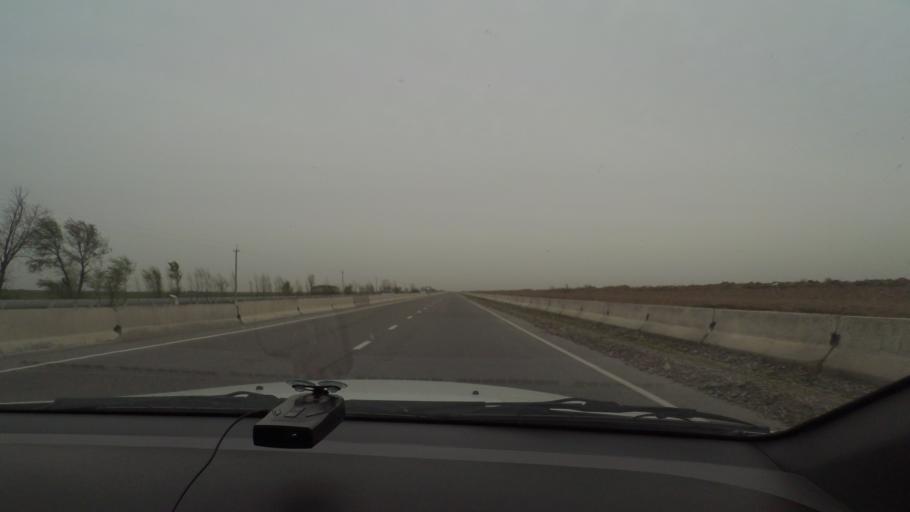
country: UZ
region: Jizzax
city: Dustlik
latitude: 40.4310
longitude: 68.2259
